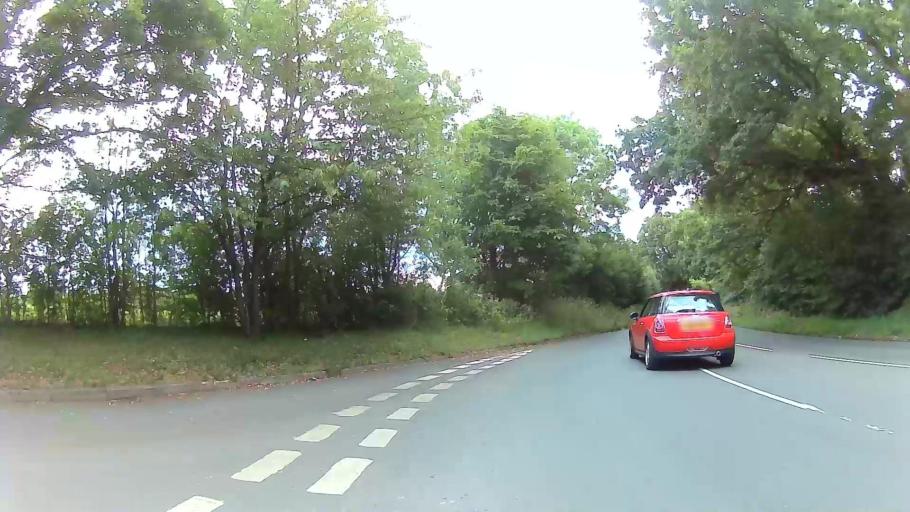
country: GB
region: England
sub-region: Greater London
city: Hainault
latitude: 51.6340
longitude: 0.1392
